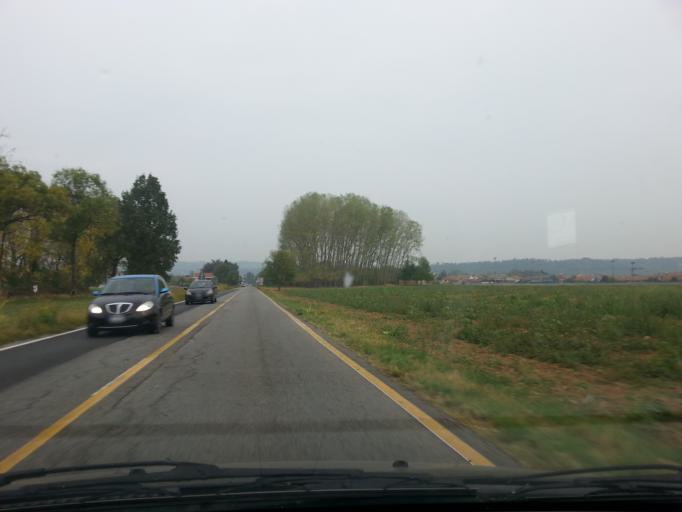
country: IT
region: Piedmont
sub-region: Provincia di Torino
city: Bruino
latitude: 45.0127
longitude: 7.4657
